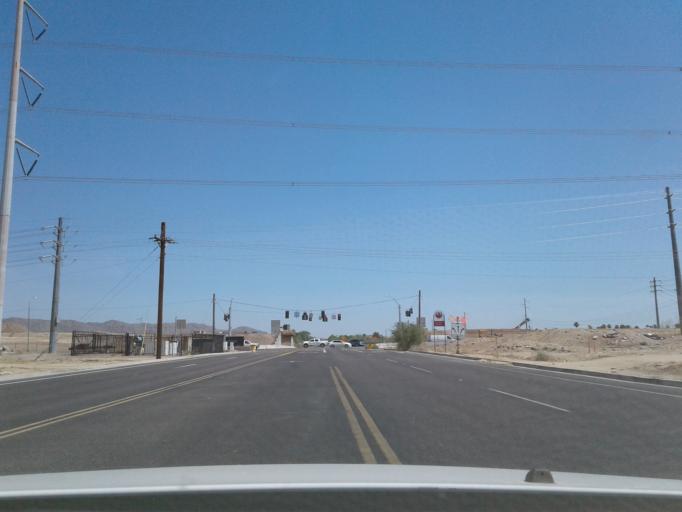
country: US
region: Arizona
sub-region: Maricopa County
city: Guadalupe
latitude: 33.2900
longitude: -111.9972
